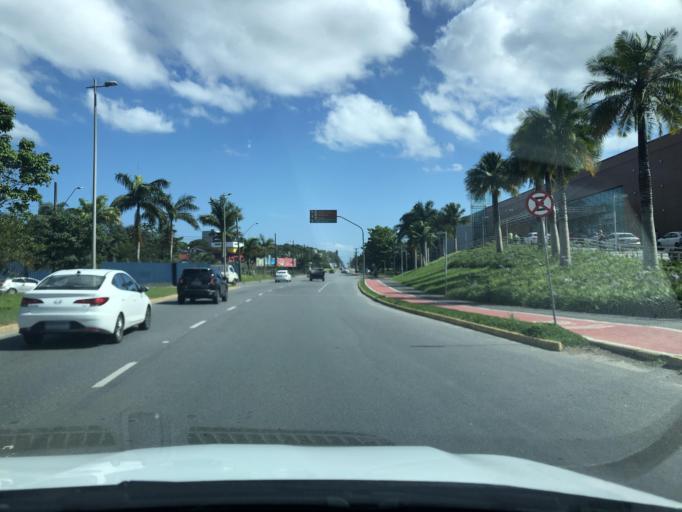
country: BR
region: Santa Catarina
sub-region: Joinville
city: Joinville
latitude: -26.2530
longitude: -48.8523
